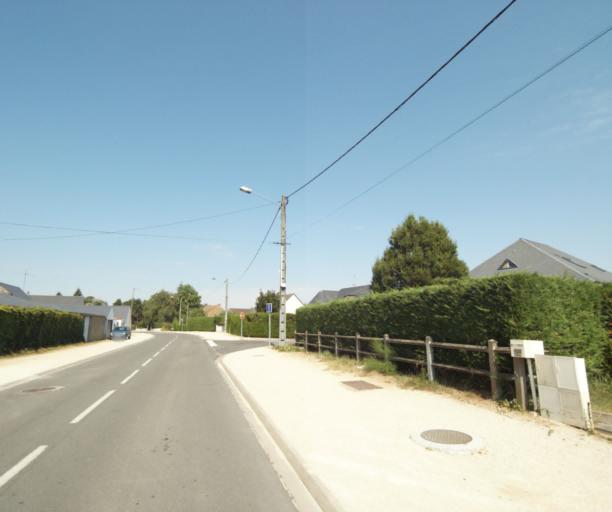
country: FR
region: Centre
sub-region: Departement du Loiret
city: Saint-Denis-en-Val
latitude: 47.8802
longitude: 1.9429
